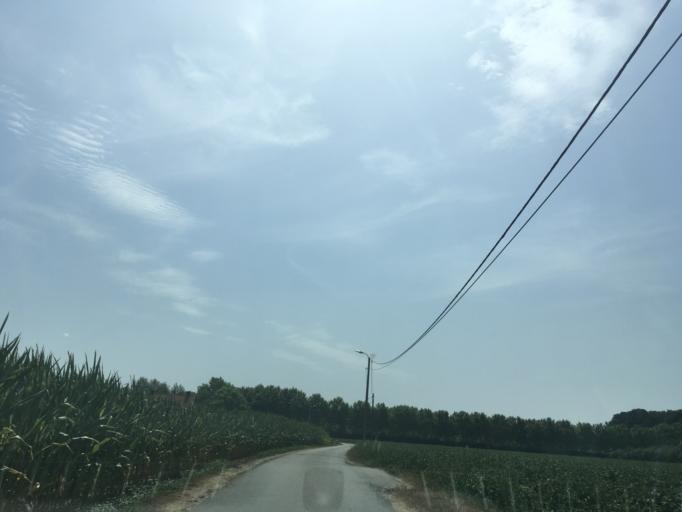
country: BE
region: Flanders
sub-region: Provincie West-Vlaanderen
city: Dentergem
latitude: 50.9803
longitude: 3.3830
